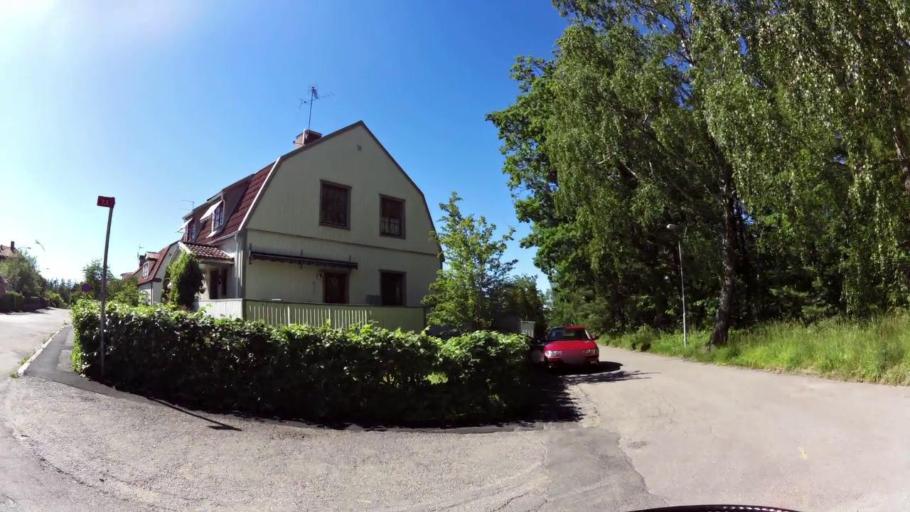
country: SE
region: OEstergoetland
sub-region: Linkopings Kommun
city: Linkoping
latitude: 58.4008
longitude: 15.6300
